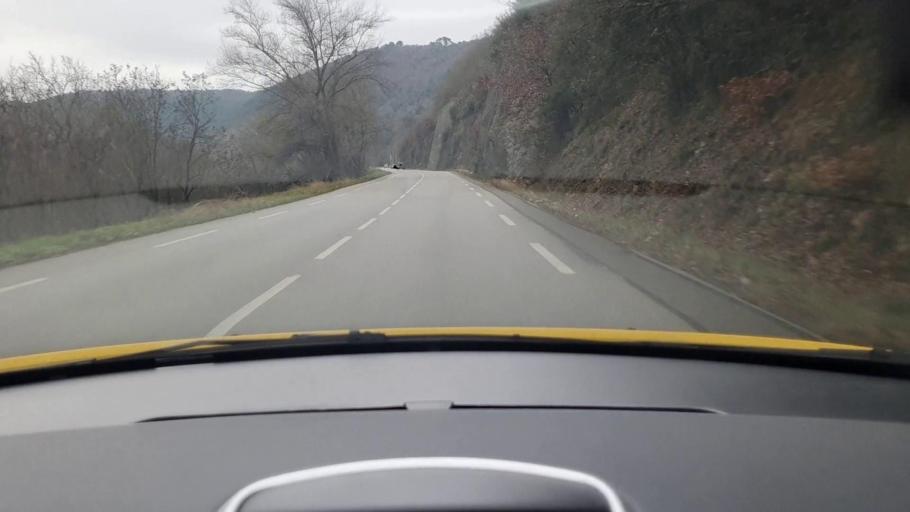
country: FR
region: Languedoc-Roussillon
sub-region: Departement du Gard
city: Molieres-sur-Ceze
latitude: 44.2706
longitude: 4.1542
